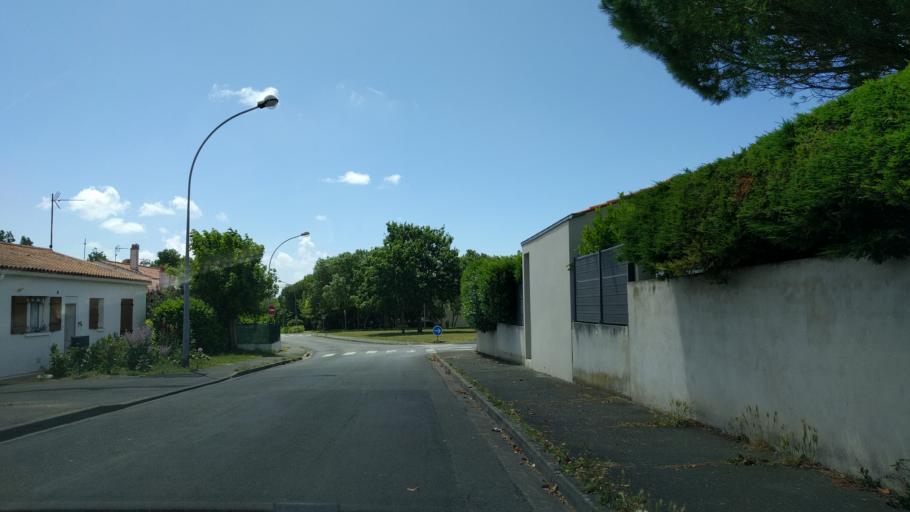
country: FR
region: Poitou-Charentes
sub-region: Departement de la Charente-Maritime
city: Puilboreau
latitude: 46.1684
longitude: -1.1240
